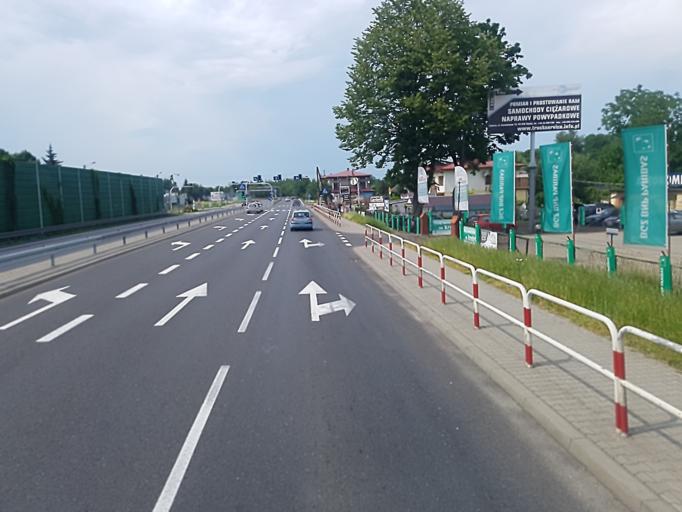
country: PL
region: Silesian Voivodeship
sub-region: Powiat cieszynski
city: Ochaby
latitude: 49.8415
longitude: 18.7698
